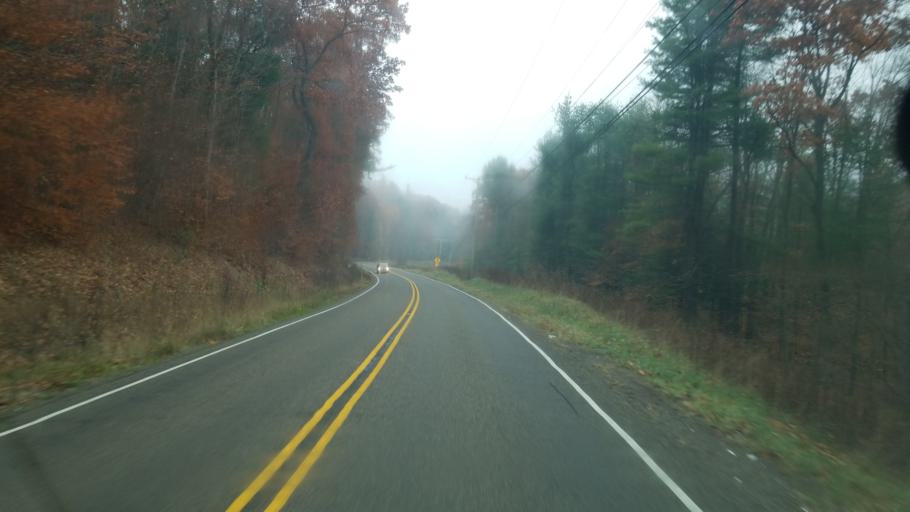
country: US
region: Pennsylvania
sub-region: McKean County
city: Foster Brook
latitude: 41.9033
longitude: -78.5257
